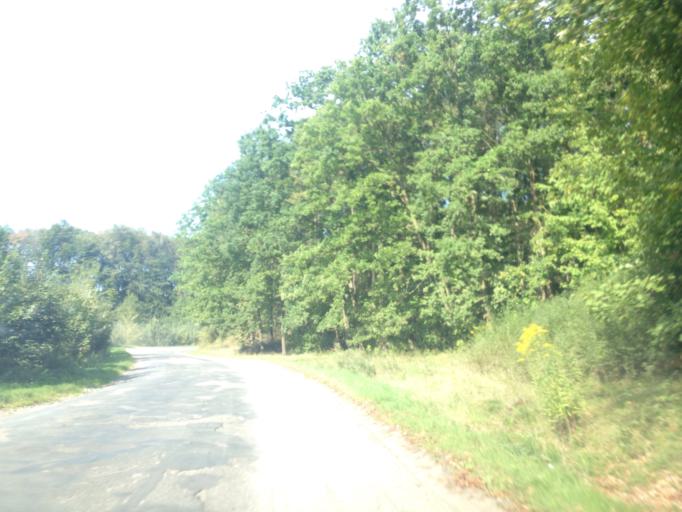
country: PL
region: Kujawsko-Pomorskie
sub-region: Powiat golubsko-dobrzynski
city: Golub-Dobrzyn
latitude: 53.1127
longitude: 19.0408
